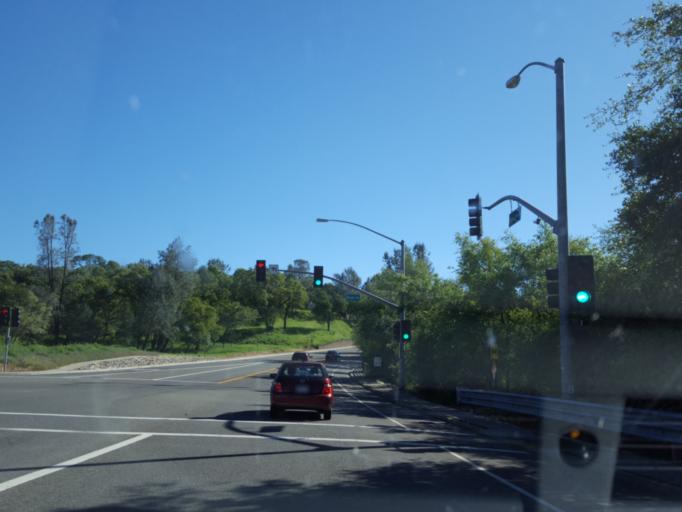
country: US
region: California
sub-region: Placer County
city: Auburn
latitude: 38.8767
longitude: -121.0810
